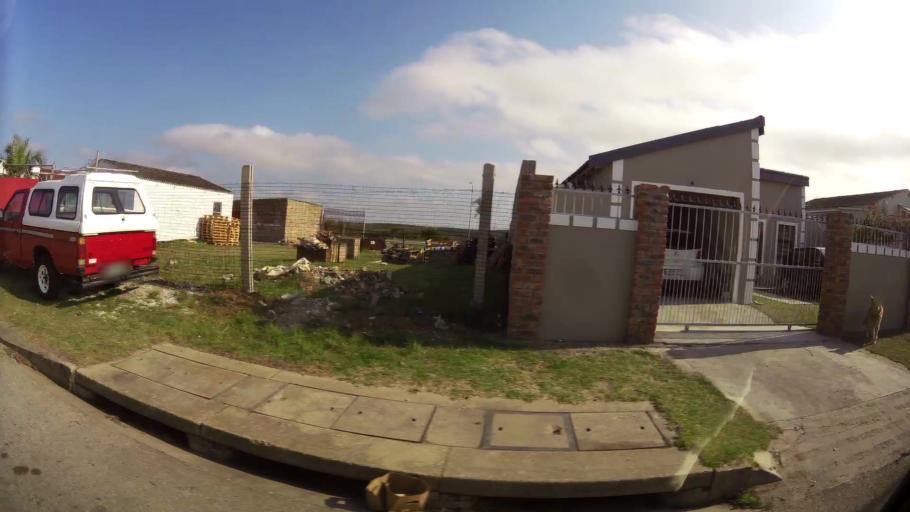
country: ZA
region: Eastern Cape
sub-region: Nelson Mandela Bay Metropolitan Municipality
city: Port Elizabeth
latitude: -33.9164
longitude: 25.5342
